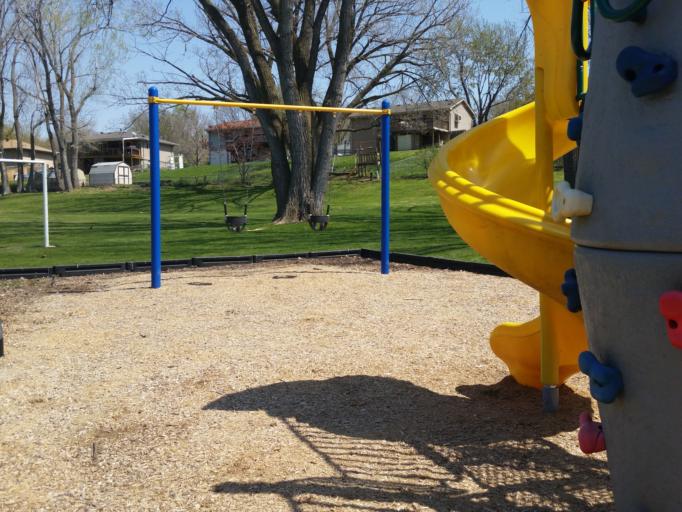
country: US
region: Nebraska
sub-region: Sarpy County
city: Offutt Air Force Base
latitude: 41.1457
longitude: -95.9341
